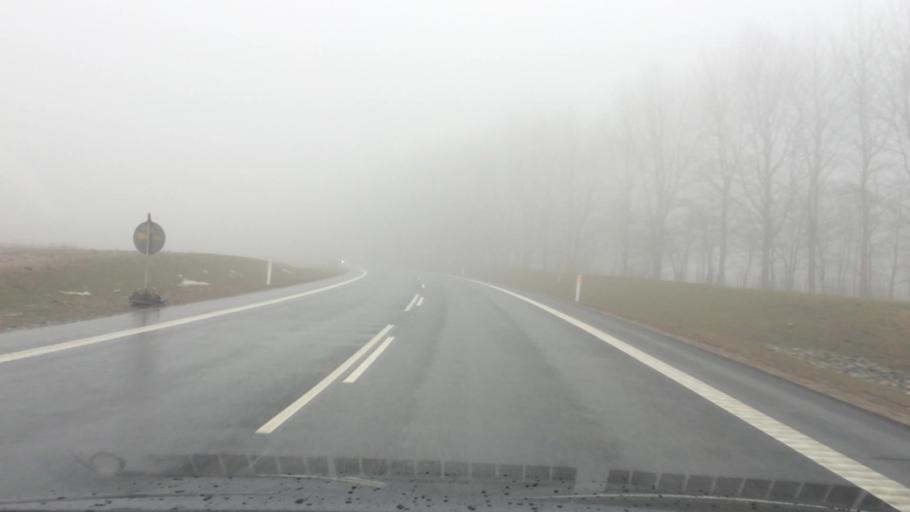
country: DK
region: Central Jutland
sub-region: Horsens Kommune
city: Horsens
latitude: 55.8620
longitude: 9.7953
